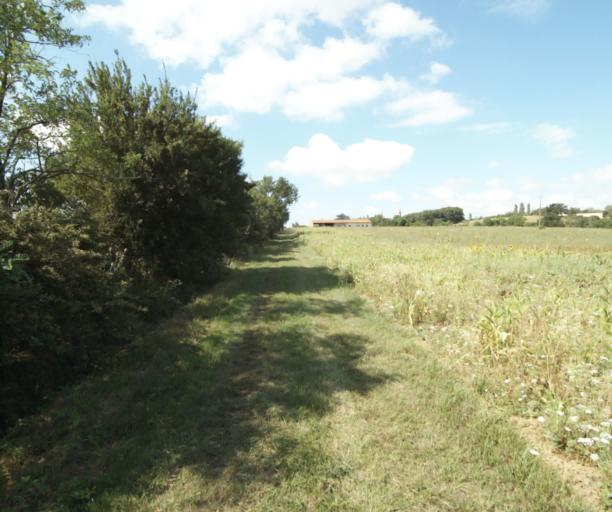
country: FR
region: Midi-Pyrenees
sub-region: Departement de la Haute-Garonne
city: Avignonet-Lauragais
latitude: 43.4396
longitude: 1.7900
